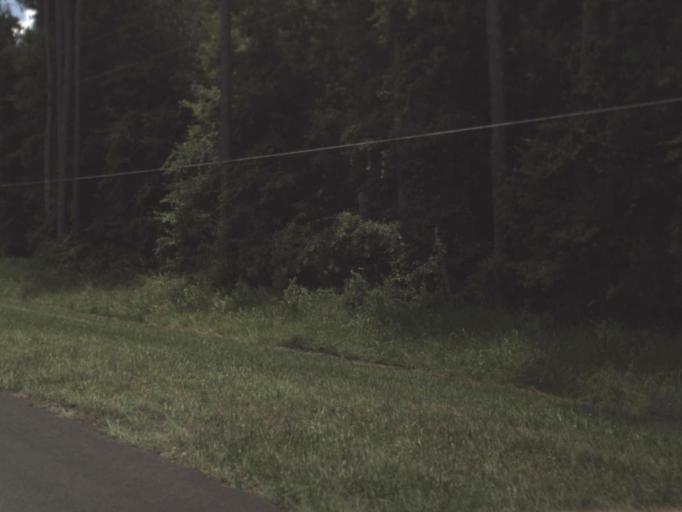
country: US
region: Florida
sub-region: Alachua County
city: Alachua
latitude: 29.7667
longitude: -82.3646
